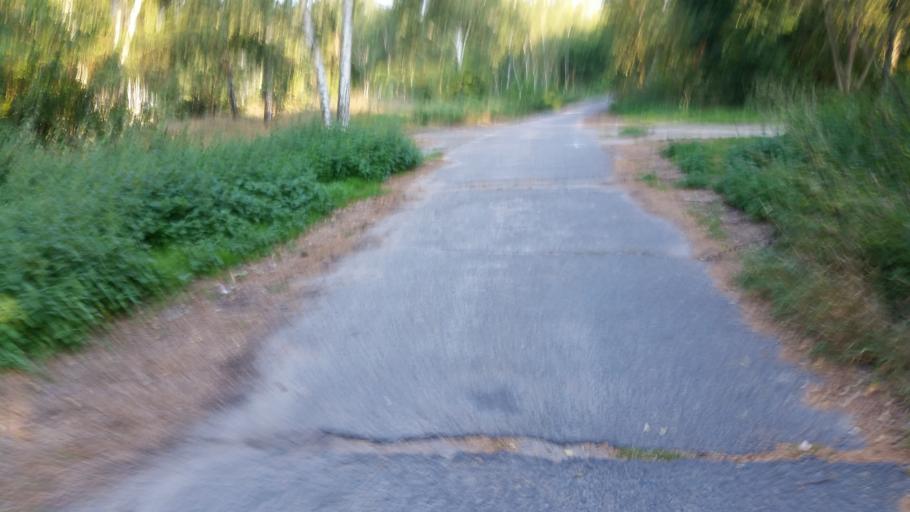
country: DE
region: Berlin
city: Marienfelde
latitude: 52.4083
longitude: 13.3413
